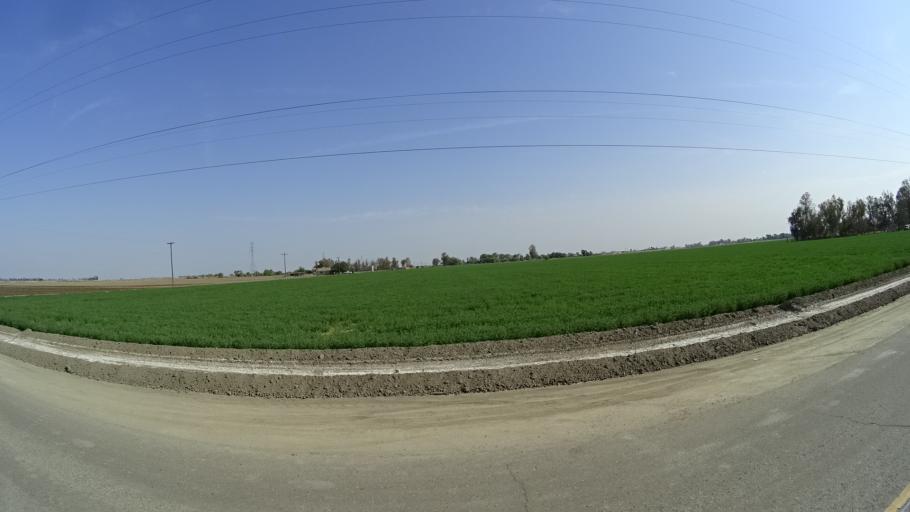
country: US
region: California
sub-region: Kings County
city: Lemoore Station
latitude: 36.3284
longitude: -119.8866
